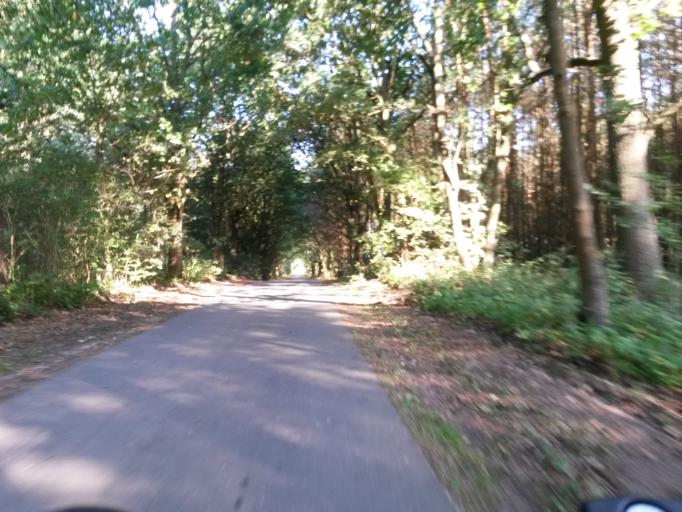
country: DE
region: Brandenburg
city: Templin
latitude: 53.1335
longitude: 13.4514
